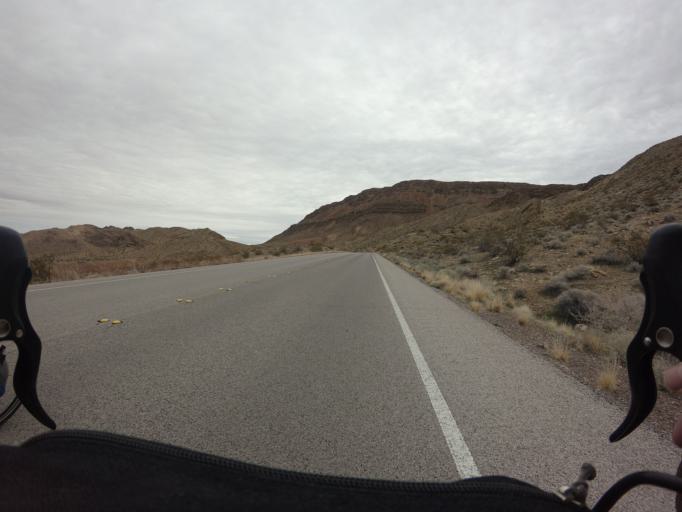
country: US
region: Nevada
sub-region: Clark County
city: Moapa Valley
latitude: 36.2329
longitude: -114.5693
